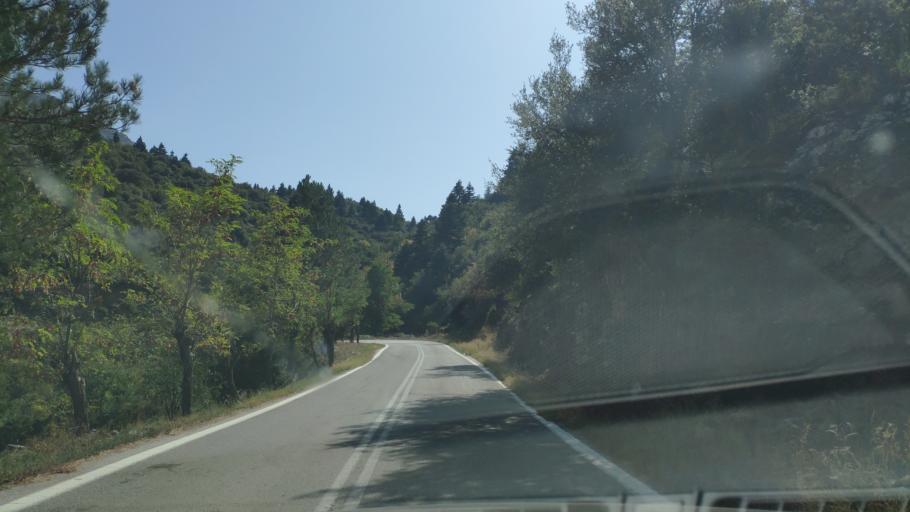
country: GR
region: West Greece
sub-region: Nomos Achaias
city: Aiyira
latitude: 37.9195
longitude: 22.3368
